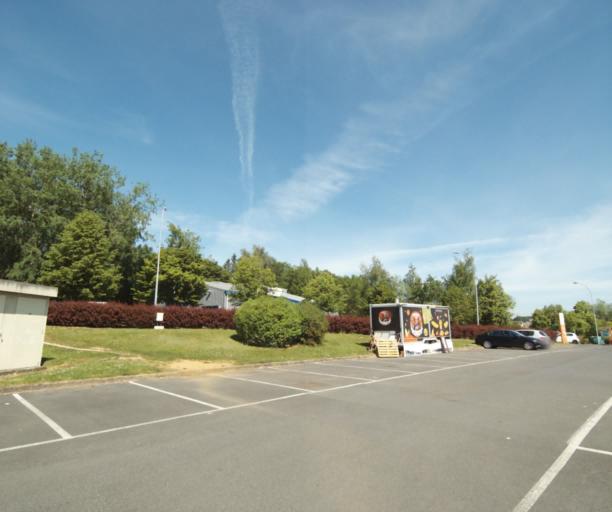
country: FR
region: Champagne-Ardenne
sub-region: Departement des Ardennes
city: Villers-Semeuse
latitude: 49.7459
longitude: 4.7280
